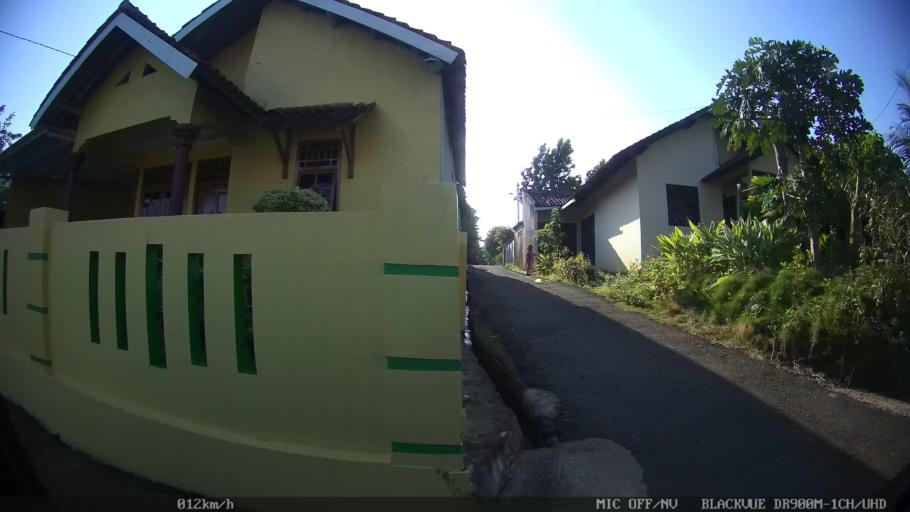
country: ID
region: Lampung
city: Kedaton
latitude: -5.3720
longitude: 105.2307
